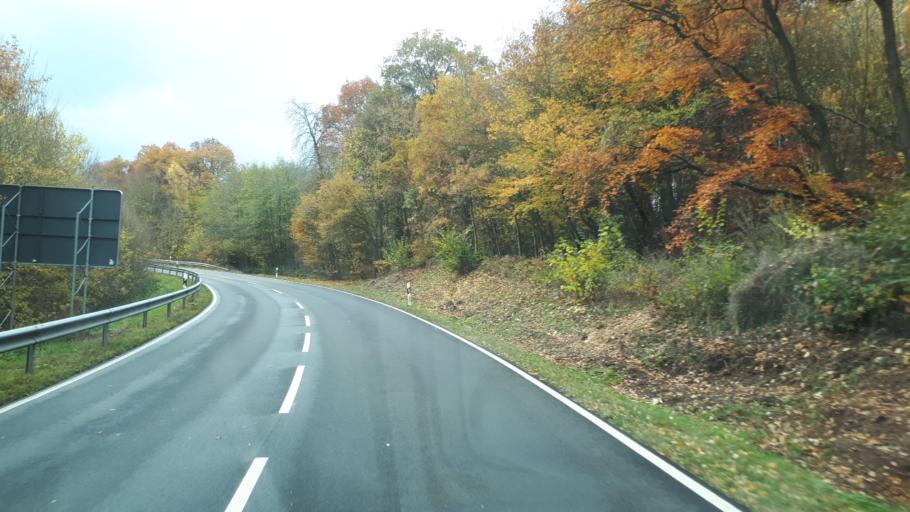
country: DE
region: Rheinland-Pfalz
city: Monreal
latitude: 50.3181
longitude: 7.1878
